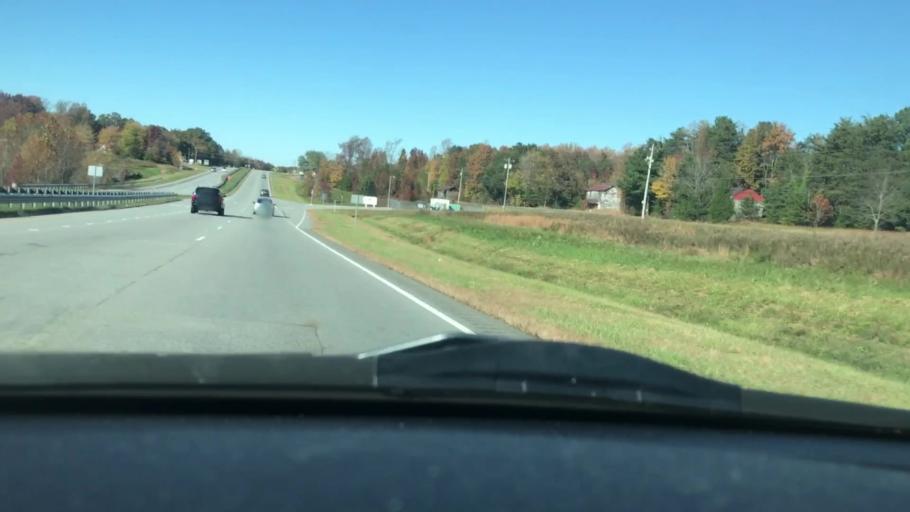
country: US
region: North Carolina
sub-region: Rockingham County
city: Madison
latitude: 36.3199
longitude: -79.9444
